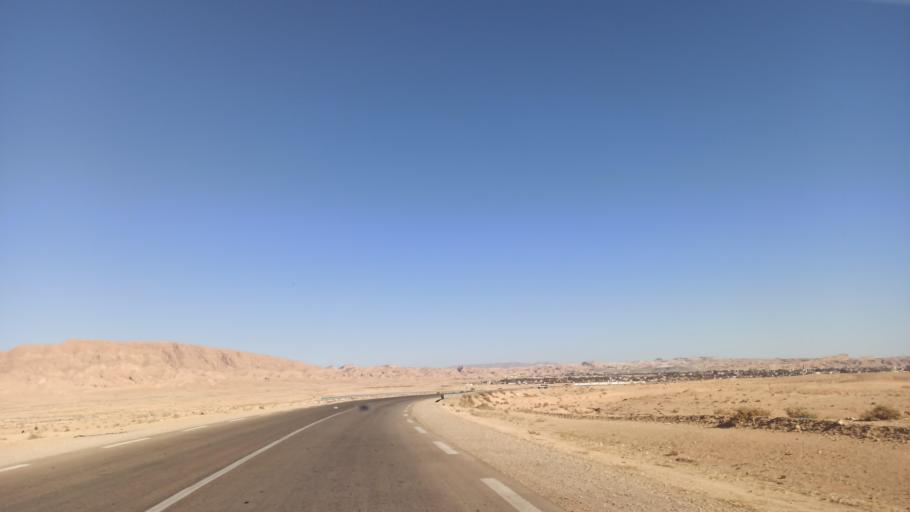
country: TN
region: Gafsa
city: Al Metlaoui
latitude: 34.3015
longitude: 8.3606
